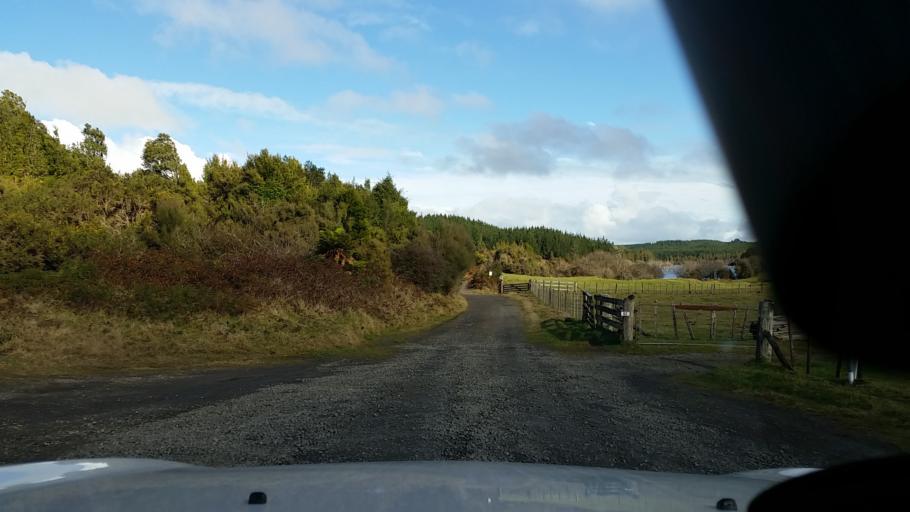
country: NZ
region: Bay of Plenty
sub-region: Rotorua District
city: Rotorua
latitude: -37.9893
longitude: 176.1630
